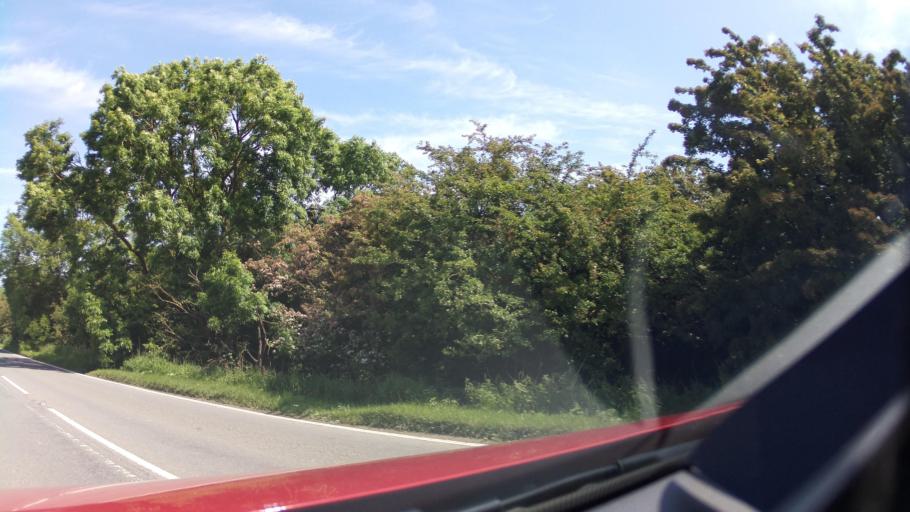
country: GB
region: England
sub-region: North Lincolnshire
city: Manton
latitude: 53.5053
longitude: -0.5824
